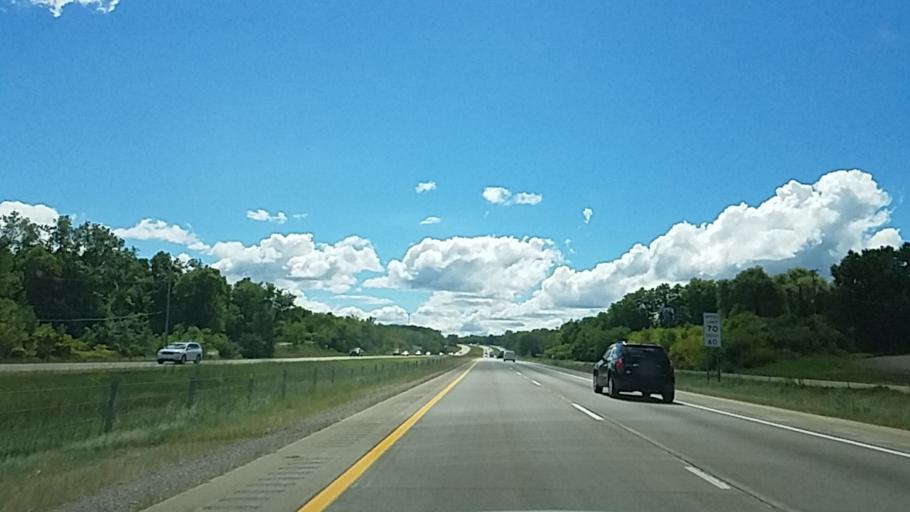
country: US
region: Michigan
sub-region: Genesee County
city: Linden
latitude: 42.7607
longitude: -83.7577
